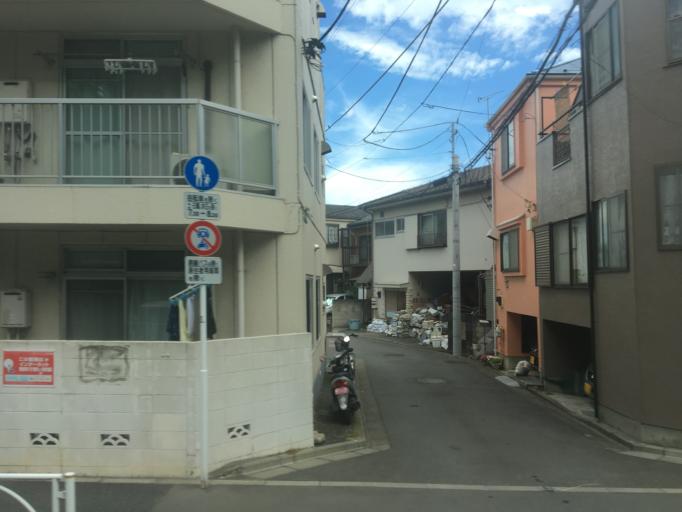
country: JP
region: Tokyo
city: Higashimurayama-shi
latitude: 35.7627
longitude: 139.4924
